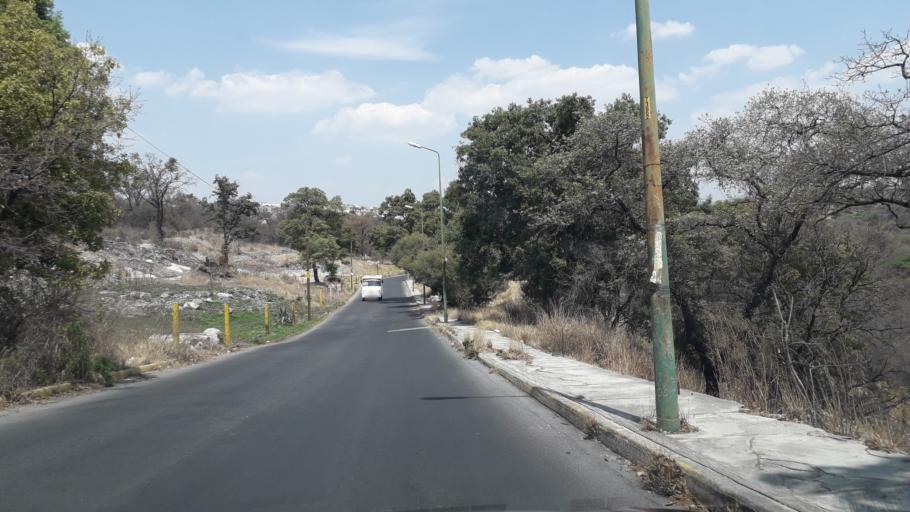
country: MX
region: Puebla
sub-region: Puebla
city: Galaxia la Calera
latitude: 18.9940
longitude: -98.1600
